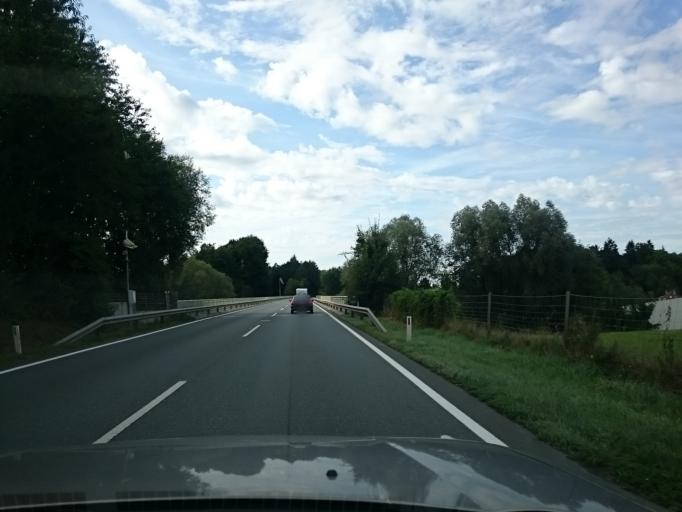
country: AT
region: Salzburg
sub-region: Politischer Bezirk Salzburg-Umgebung
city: Oberndorf bei Salzburg
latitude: 47.9351
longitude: 12.9604
